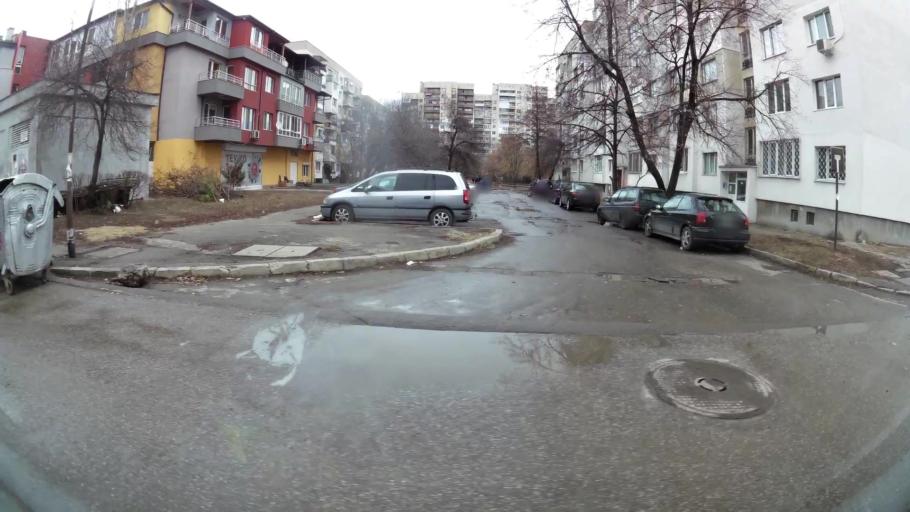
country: BG
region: Sofiya
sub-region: Obshtina Bozhurishte
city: Bozhurishte
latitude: 42.7287
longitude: 23.2509
